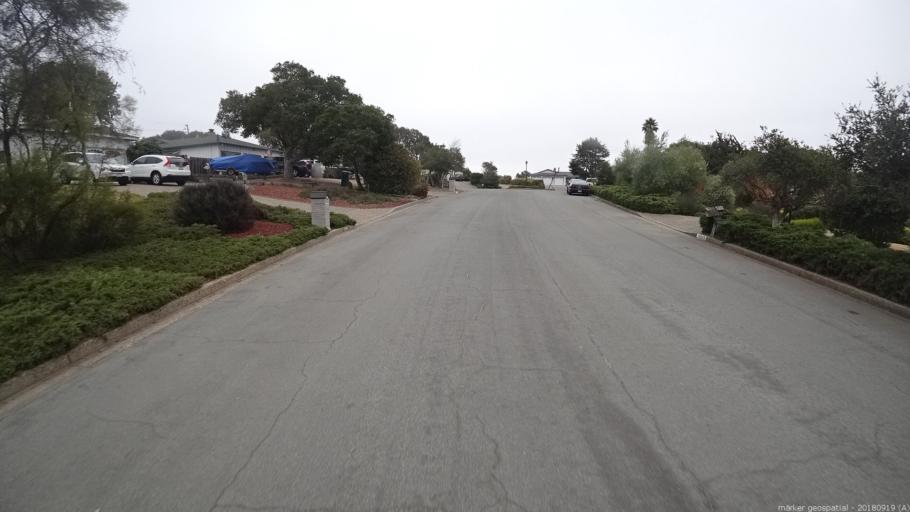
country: US
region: California
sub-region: Monterey County
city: Prunedale
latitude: 36.7819
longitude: -121.7001
